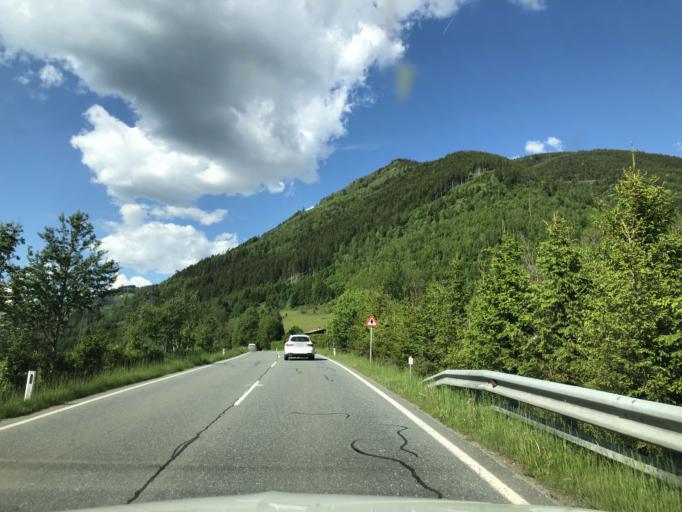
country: AT
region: Salzburg
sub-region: Politischer Bezirk Zell am See
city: Bruck an der Grossglocknerstrasse
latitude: 47.2917
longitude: 12.8145
